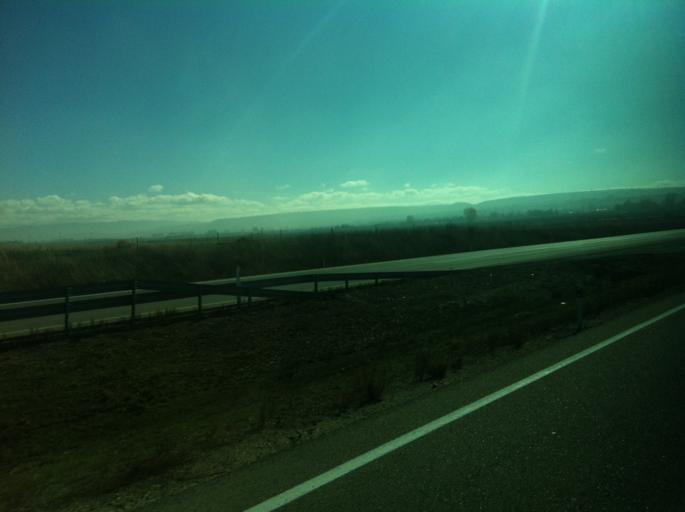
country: ES
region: Castille and Leon
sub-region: Provincia de Burgos
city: Cardenajimeno
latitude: 42.3496
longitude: -3.6034
